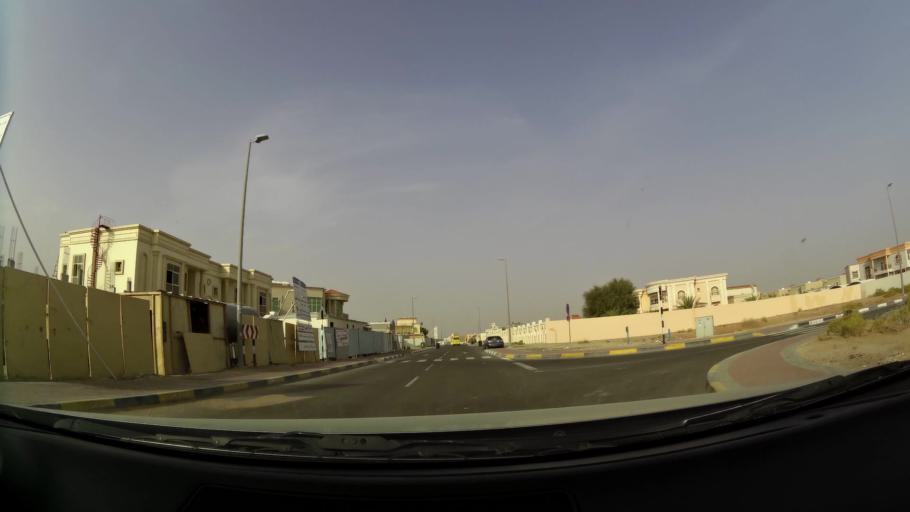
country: AE
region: Abu Dhabi
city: Al Ain
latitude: 24.1210
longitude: 55.6967
